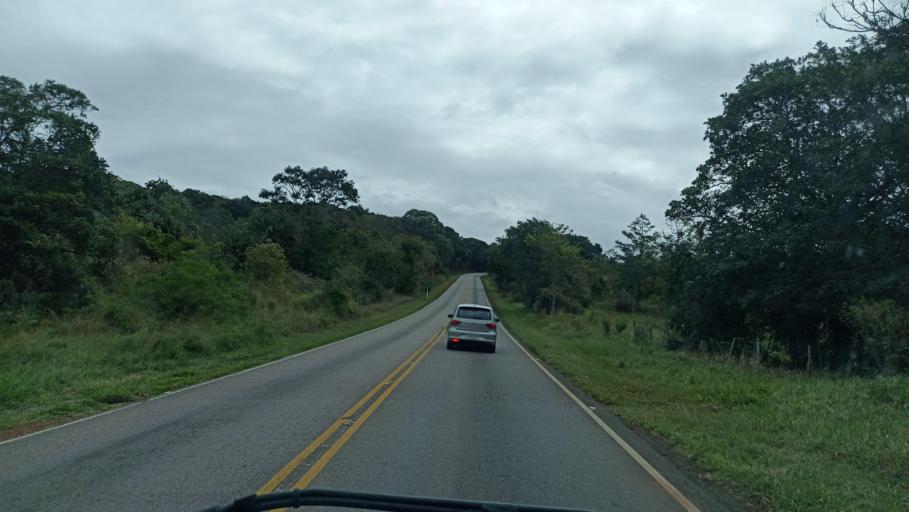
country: BR
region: Bahia
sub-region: Andarai
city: Vera Cruz
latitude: -12.9299
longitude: -41.2480
